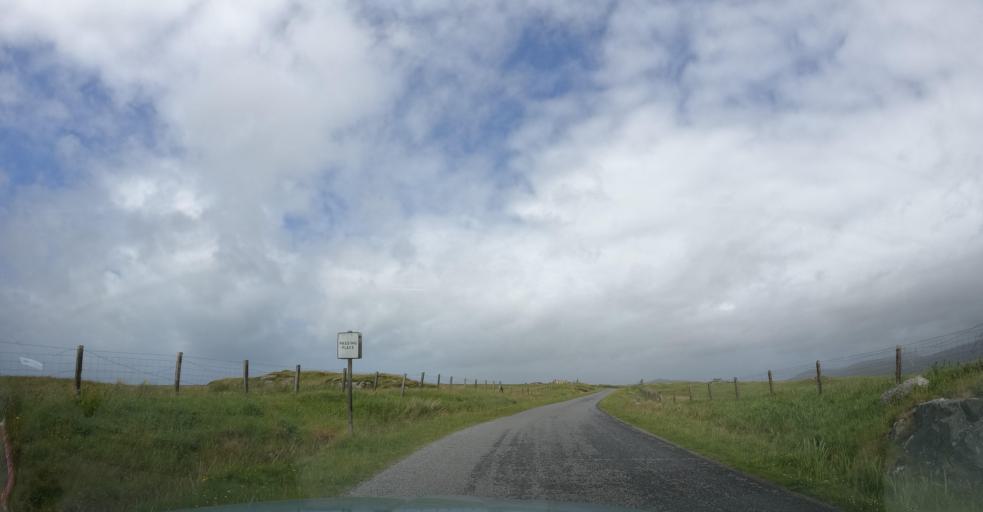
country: GB
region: Scotland
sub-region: Eilean Siar
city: Isle of South Uist
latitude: 57.2430
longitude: -7.4068
